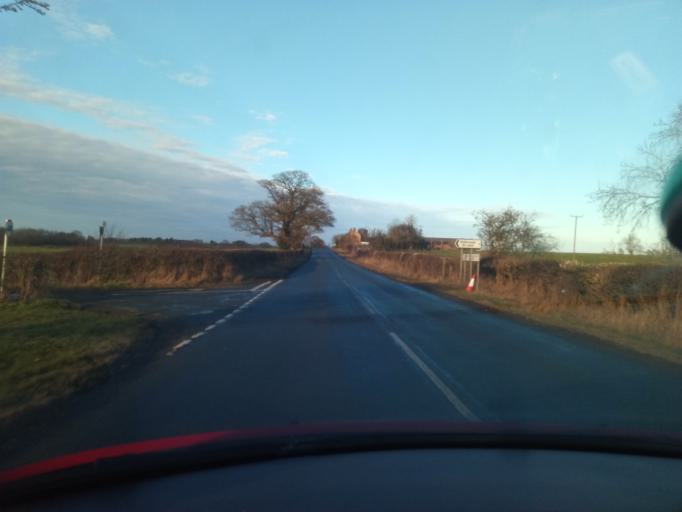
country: GB
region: England
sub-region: Darlington
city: High Coniscliffe
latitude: 54.4959
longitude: -1.6706
